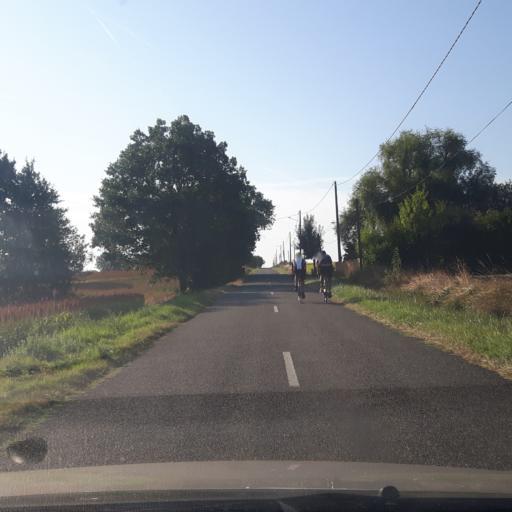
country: FR
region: Midi-Pyrenees
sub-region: Departement de la Haute-Garonne
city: Vacquiers
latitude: 43.7635
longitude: 1.4956
